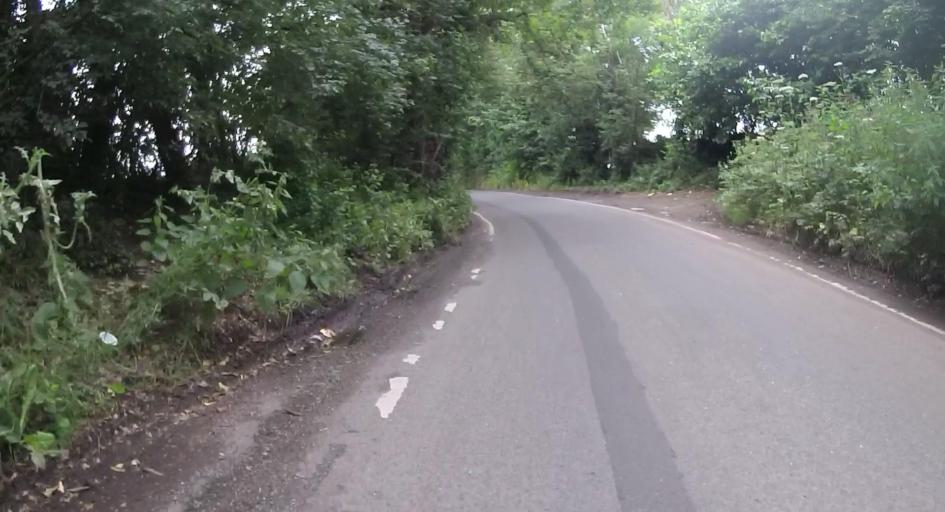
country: GB
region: England
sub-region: Wokingham
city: Barkham
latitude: 51.3891
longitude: -0.8776
